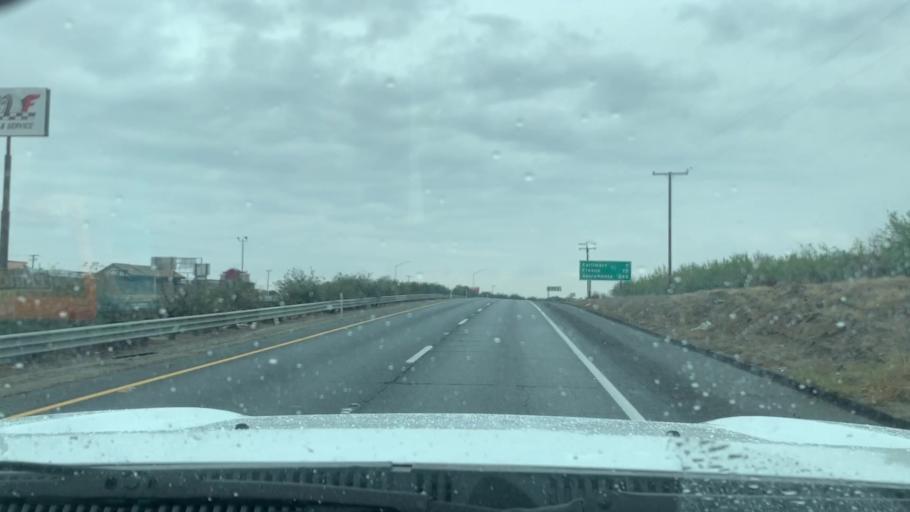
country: US
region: California
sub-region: Kern County
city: Delano
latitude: 35.7920
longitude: -119.2517
